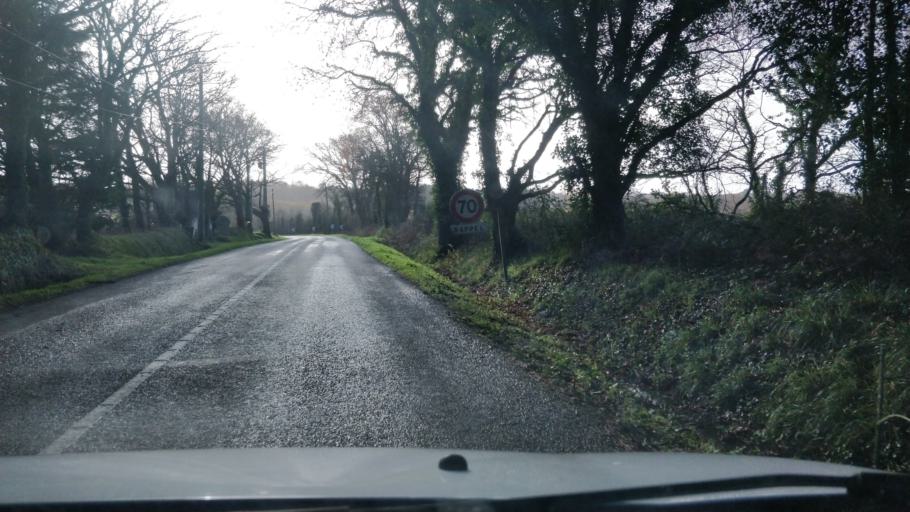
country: FR
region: Pays de la Loire
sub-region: Departement de la Loire-Atlantique
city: Saint-Molf
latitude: 47.3707
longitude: -2.4334
